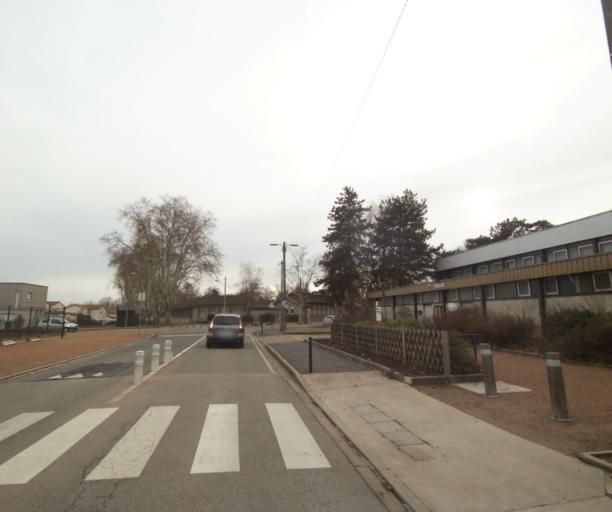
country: FR
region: Rhone-Alpes
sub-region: Departement de la Loire
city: Mably
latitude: 46.0648
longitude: 4.0786
